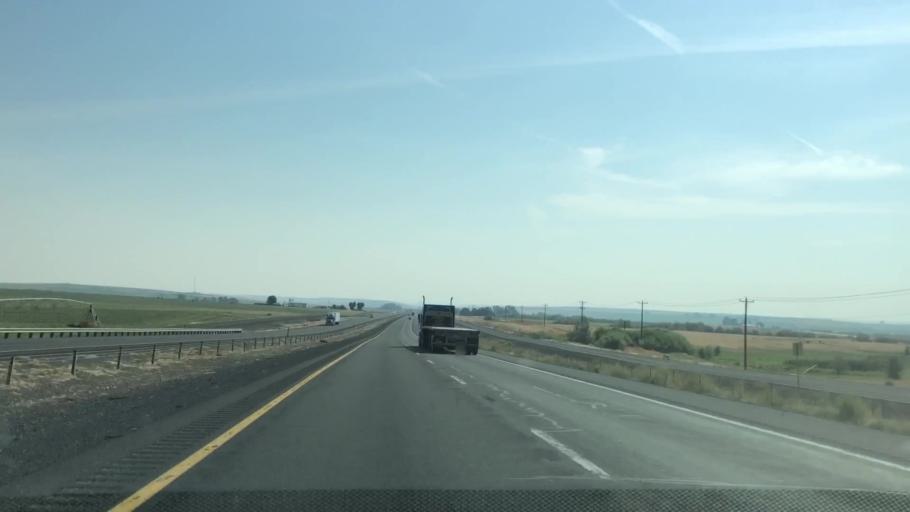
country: US
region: Washington
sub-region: Grant County
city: Warden
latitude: 47.0861
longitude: -119.0785
